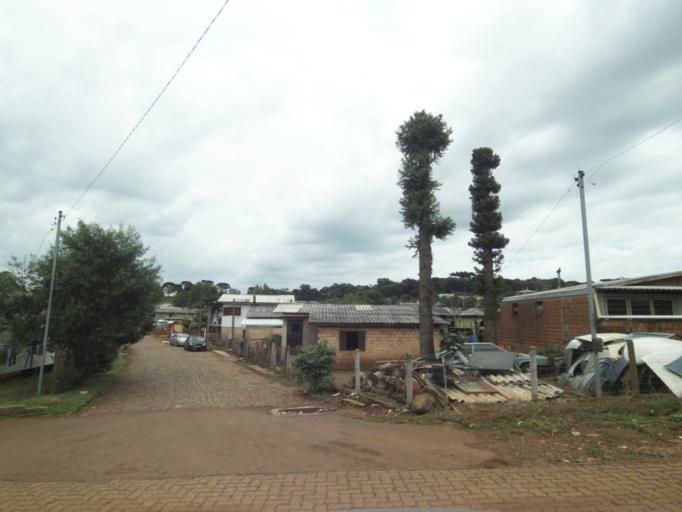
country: BR
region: Rio Grande do Sul
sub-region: Lagoa Vermelha
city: Lagoa Vermelha
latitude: -28.2274
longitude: -51.5133
